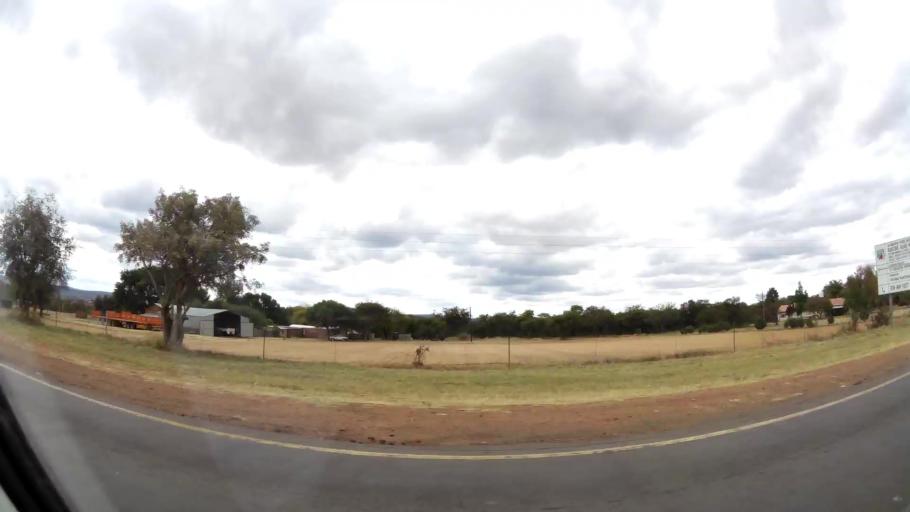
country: ZA
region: Limpopo
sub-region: Waterberg District Municipality
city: Modimolle
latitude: -24.7258
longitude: 28.4271
